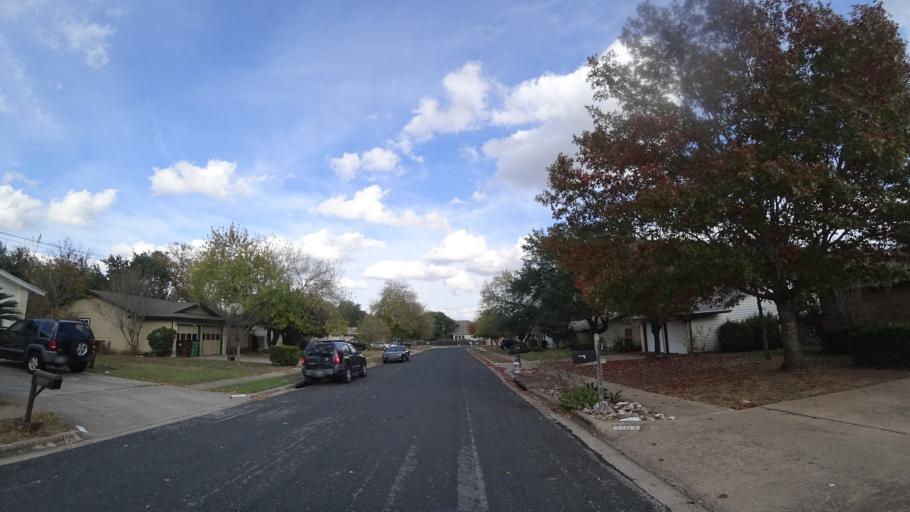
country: US
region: Texas
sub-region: Williamson County
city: Brushy Creek
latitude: 30.5114
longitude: -97.7257
